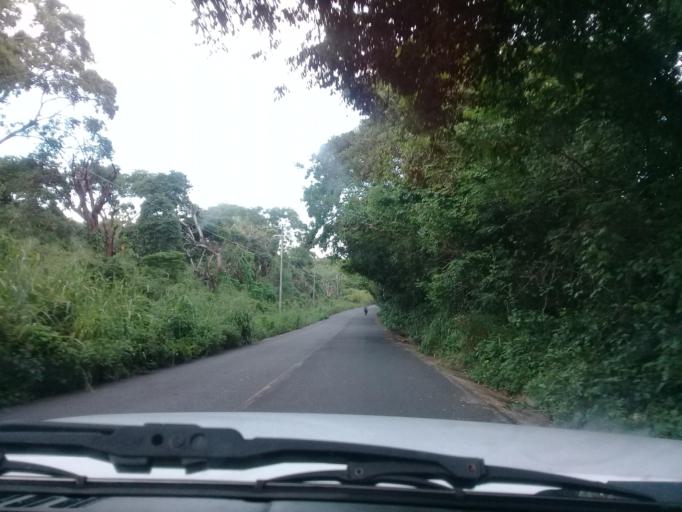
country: MX
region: Veracruz
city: Catemaco
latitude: 18.4334
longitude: -95.0909
